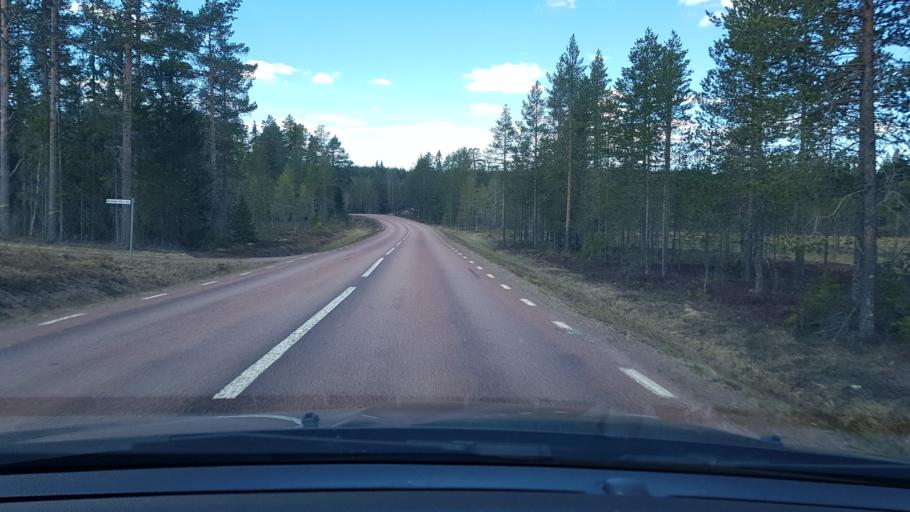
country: SE
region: Dalarna
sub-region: Malung-Saelens kommun
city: Malung
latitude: 61.0668
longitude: 13.4767
